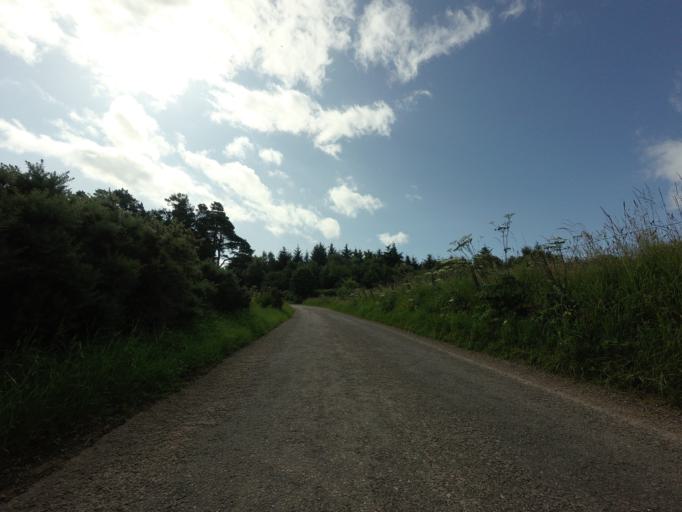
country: GB
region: Scotland
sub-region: Highland
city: Nairn
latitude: 57.5596
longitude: -3.8678
